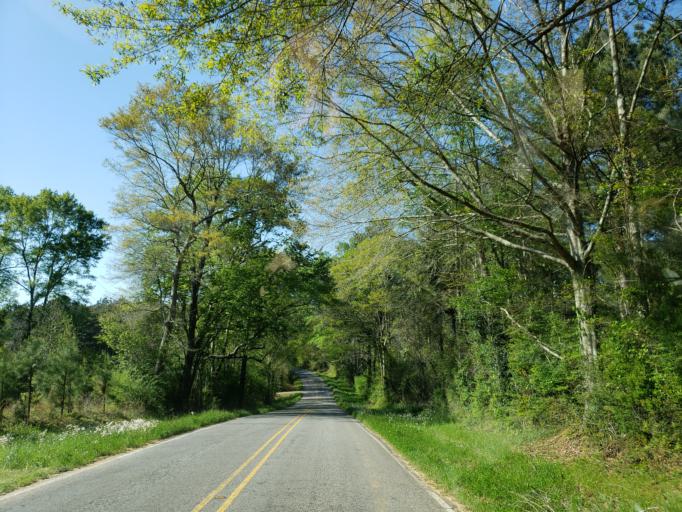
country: US
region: Mississippi
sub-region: Forrest County
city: Rawls Springs
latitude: 31.5336
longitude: -89.3606
